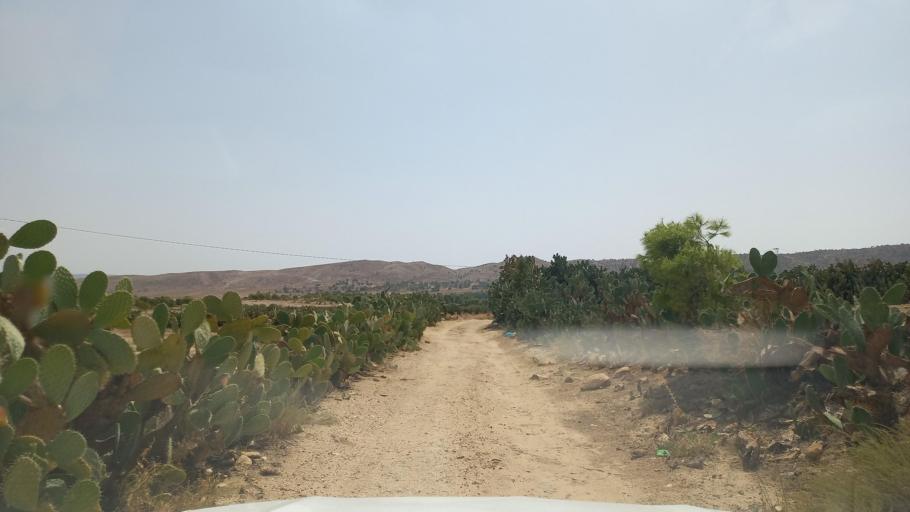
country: TN
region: Al Qasrayn
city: Sbiba
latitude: 35.3977
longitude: 8.9830
